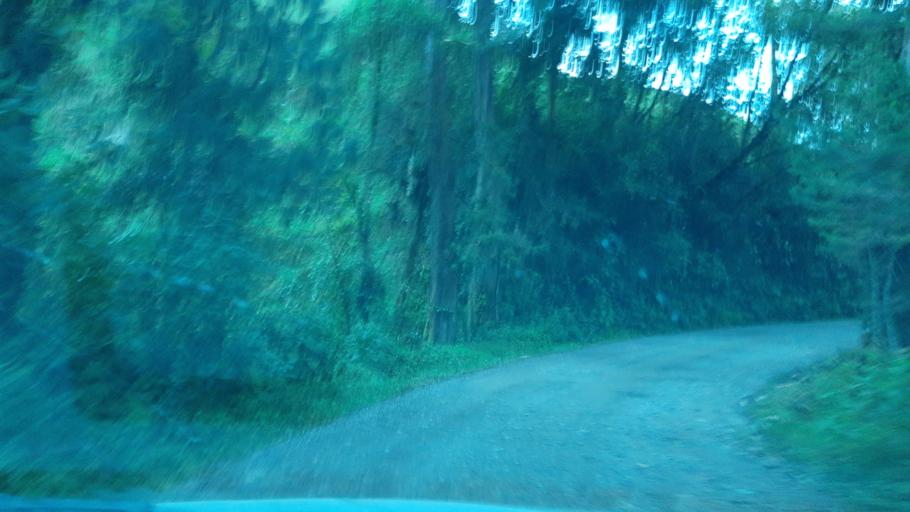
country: CO
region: Boyaca
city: Garagoa
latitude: 5.0905
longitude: -73.3333
